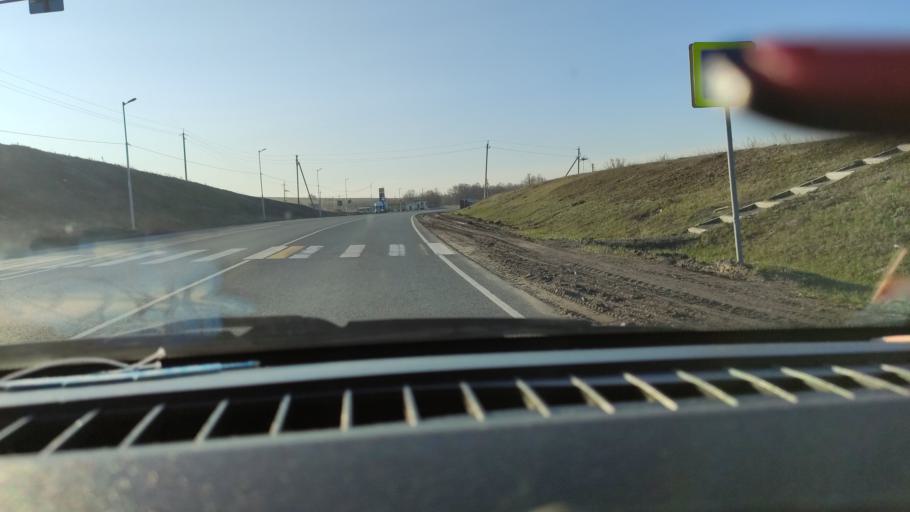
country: RU
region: Saratov
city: Tersa
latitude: 52.0951
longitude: 47.5395
